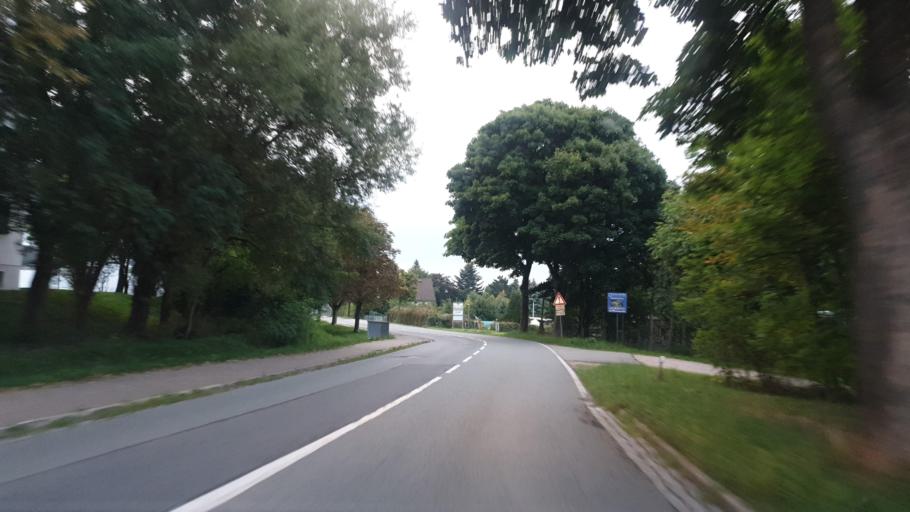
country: DE
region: Saxony
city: Eibenstock
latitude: 50.4882
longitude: 12.6080
